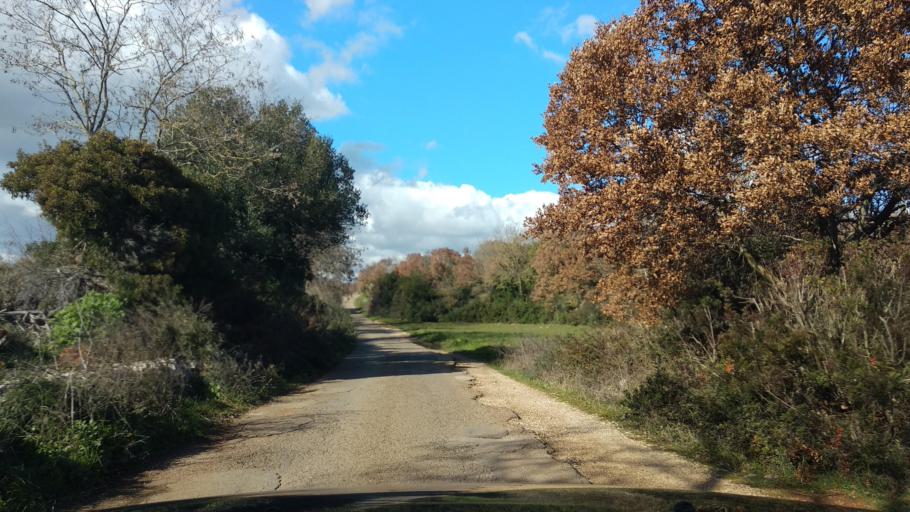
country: IT
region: Apulia
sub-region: Provincia di Brindisi
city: Casalini
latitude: 40.7159
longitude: 17.4519
